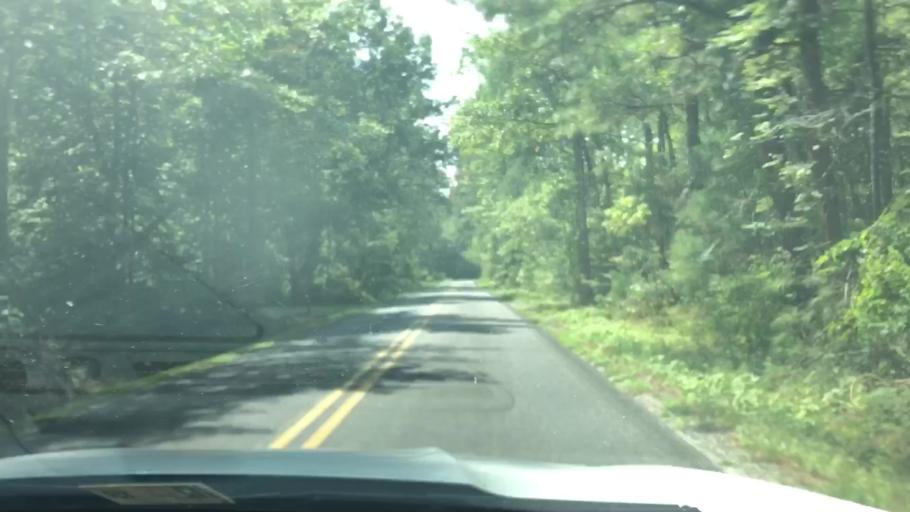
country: US
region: Virginia
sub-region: Middlesex County
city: Saluda
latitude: 37.6293
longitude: -76.7018
